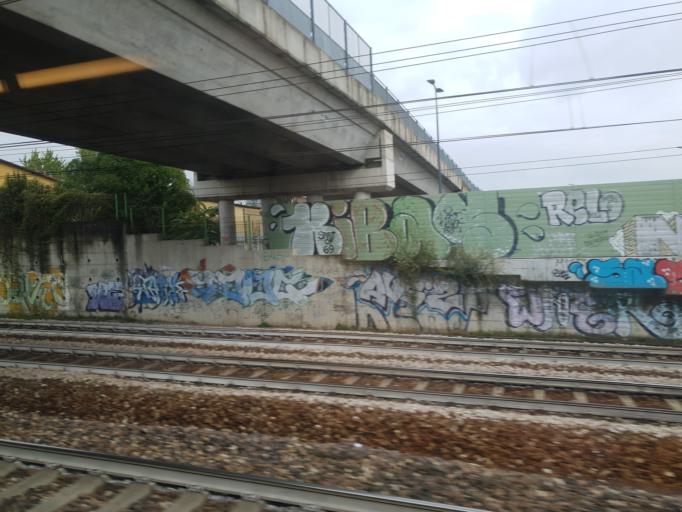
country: IT
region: Lombardy
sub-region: Citta metropolitana di Milano
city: Novate Milanese
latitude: 45.5109
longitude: 9.1526
